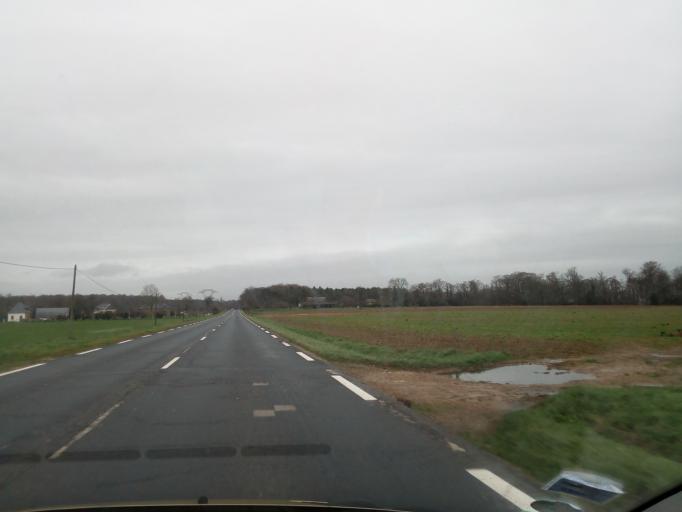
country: FR
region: Haute-Normandie
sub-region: Departement de l'Eure
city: Hauville
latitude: 49.4073
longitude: 0.7970
